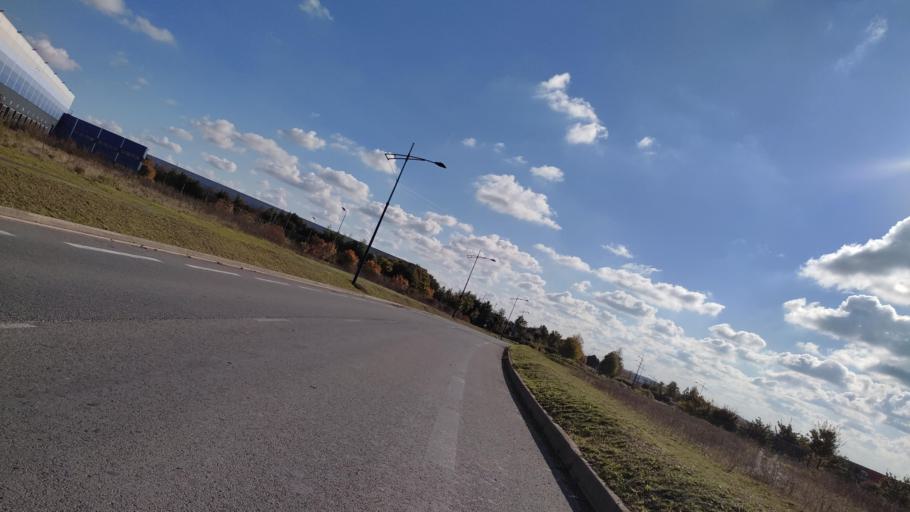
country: FR
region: Nord-Pas-de-Calais
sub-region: Departement du Pas-de-Calais
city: Feuchy
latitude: 50.3161
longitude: 2.8271
